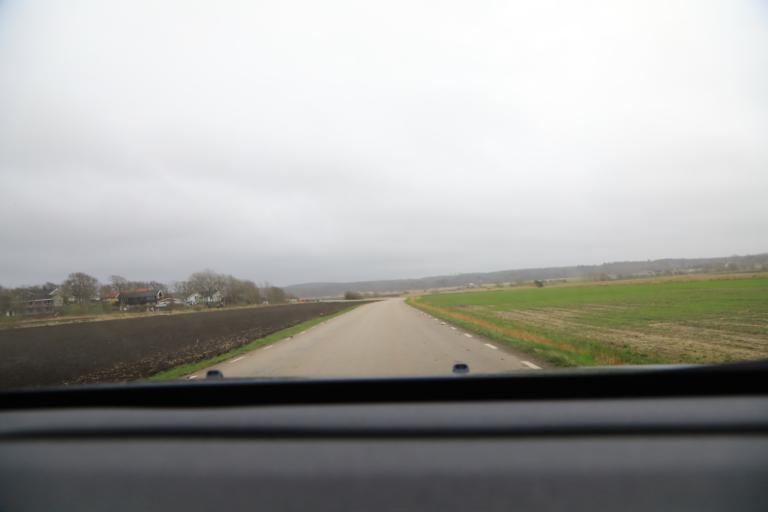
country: SE
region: Halland
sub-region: Kungsbacka Kommun
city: Frillesas
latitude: 57.2989
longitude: 12.1896
